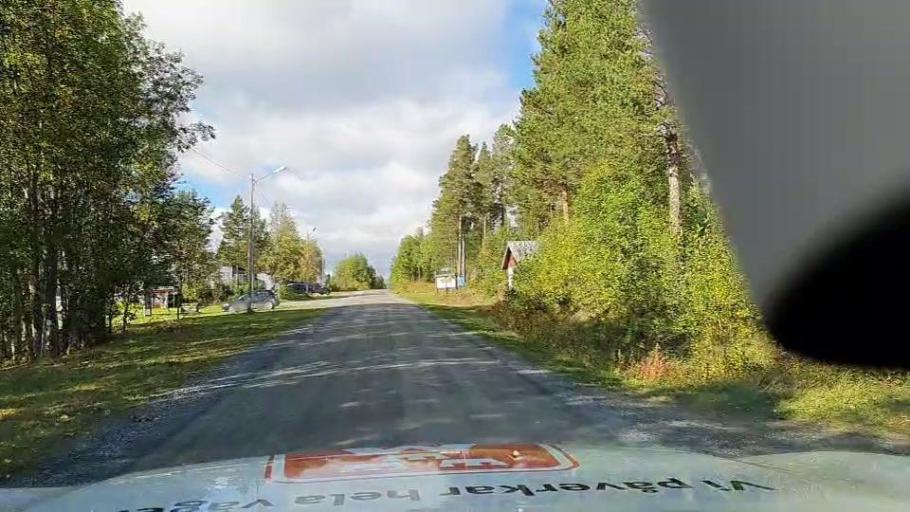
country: SE
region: Jaemtland
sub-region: Are Kommun
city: Jarpen
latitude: 63.1923
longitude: 13.6289
